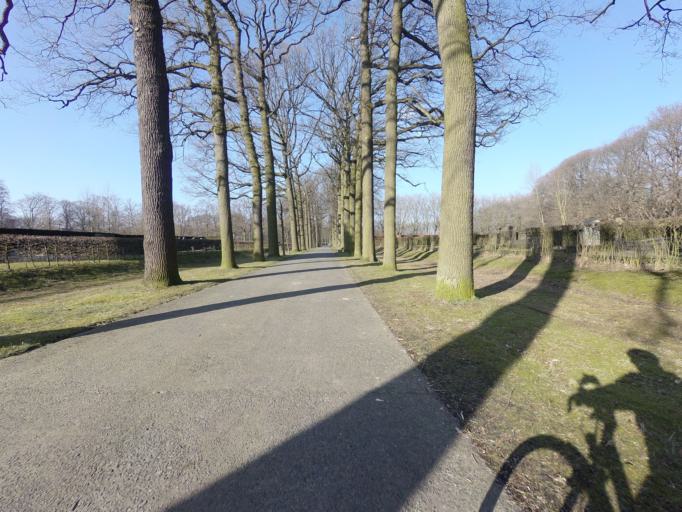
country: BE
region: Flanders
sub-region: Provincie Antwerpen
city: Hoboken
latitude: 51.1649
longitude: 4.3717
